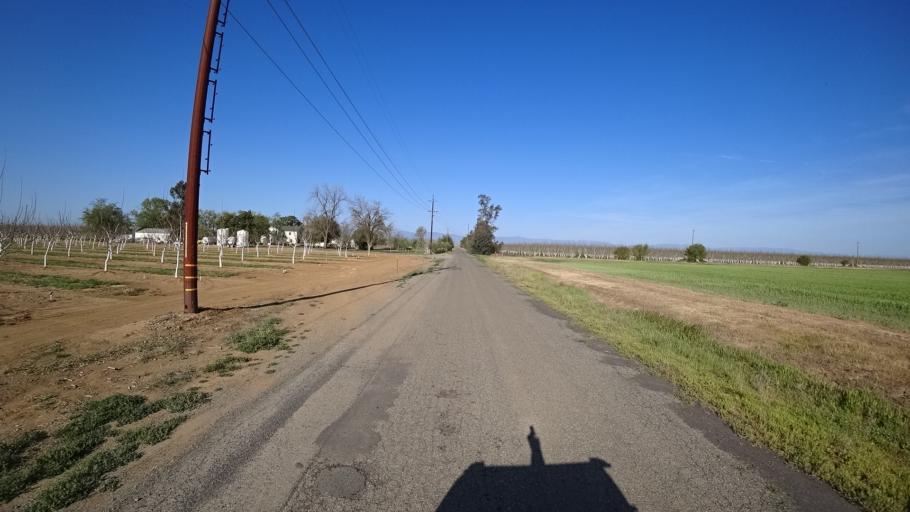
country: US
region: California
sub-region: Glenn County
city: Willows
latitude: 39.5534
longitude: -122.2299
